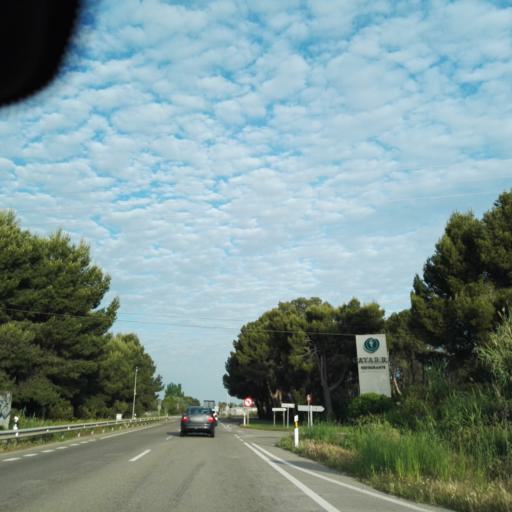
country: ES
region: Aragon
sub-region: Provincia de Zaragoza
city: Oliver-Valdefierro, Oliver, Valdefierro
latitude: 41.6635
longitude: -0.9813
